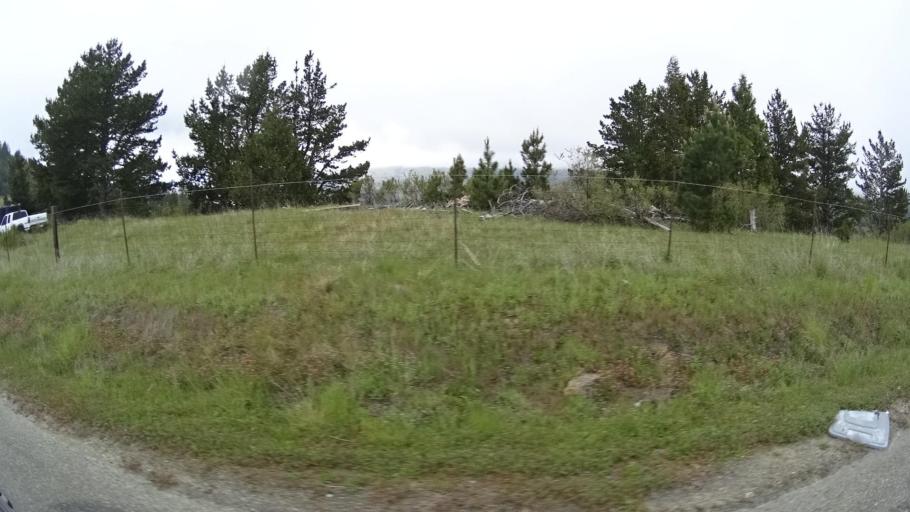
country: US
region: California
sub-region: Humboldt County
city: Redway
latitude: 40.1124
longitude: -123.7251
